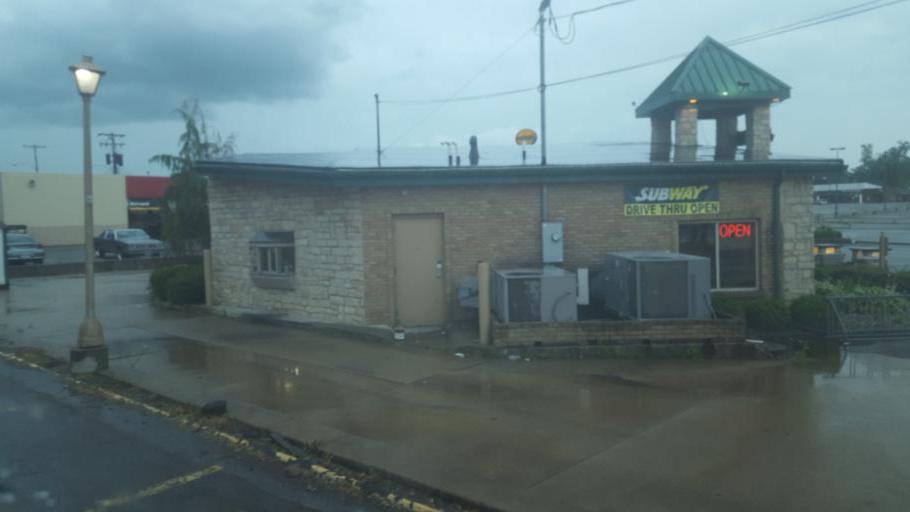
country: US
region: Ohio
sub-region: Richland County
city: Ontario
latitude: 40.7590
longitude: -82.5577
